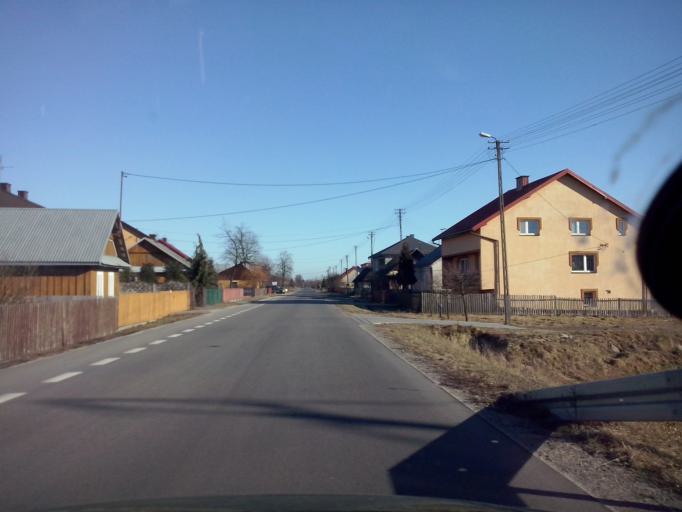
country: PL
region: Subcarpathian Voivodeship
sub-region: Powiat nizanski
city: Harasiuki
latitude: 50.4715
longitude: 22.4954
